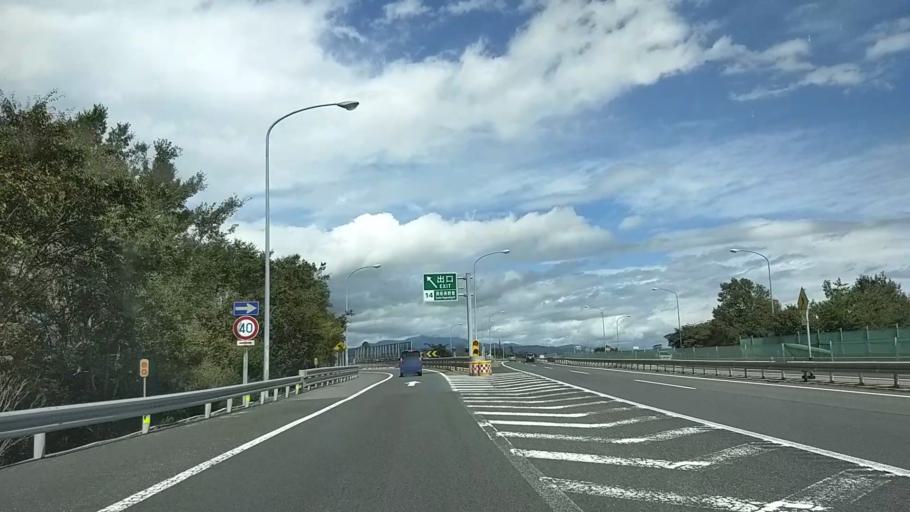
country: JP
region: Nagano
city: Suzaka
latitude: 36.6318
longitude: 138.2731
